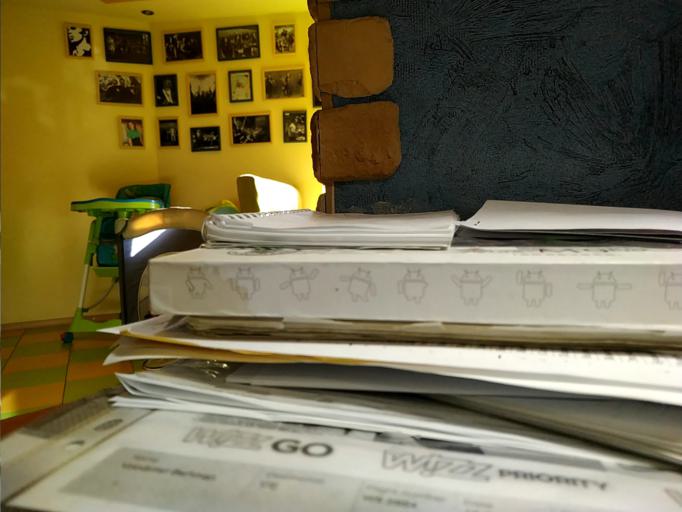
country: RU
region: Novgorod
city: Poddor'ye
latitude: 57.5980
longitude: 30.8096
